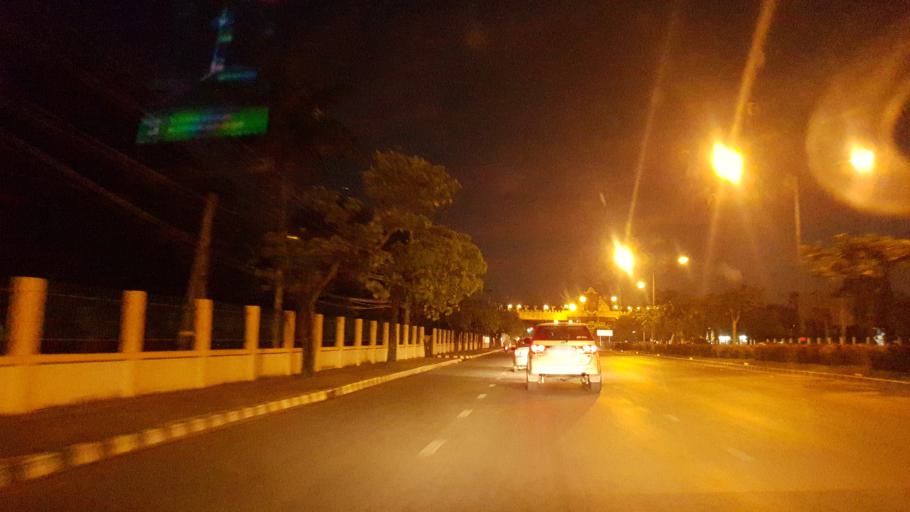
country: TH
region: Phitsanulok
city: Phitsanulok
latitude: 16.8131
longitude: 100.2723
